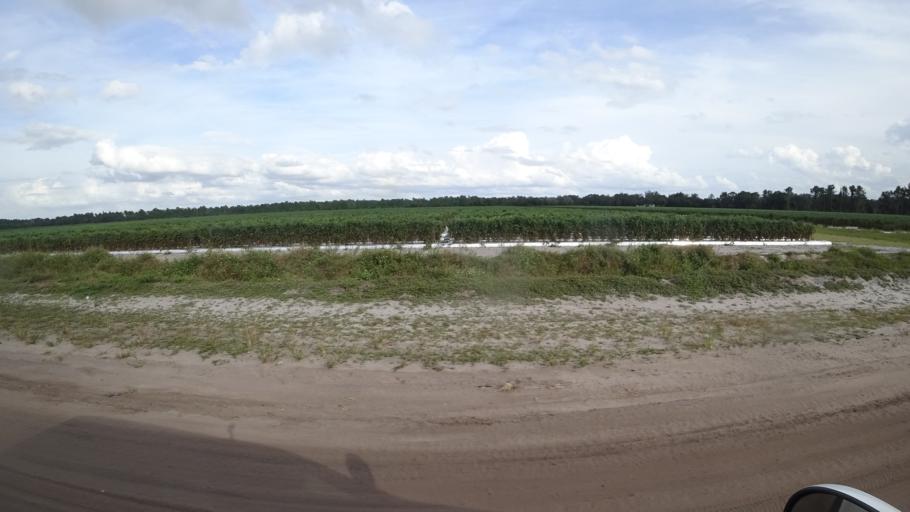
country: US
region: Florida
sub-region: Hillsborough County
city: Wimauma
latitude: 27.6131
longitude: -82.1332
